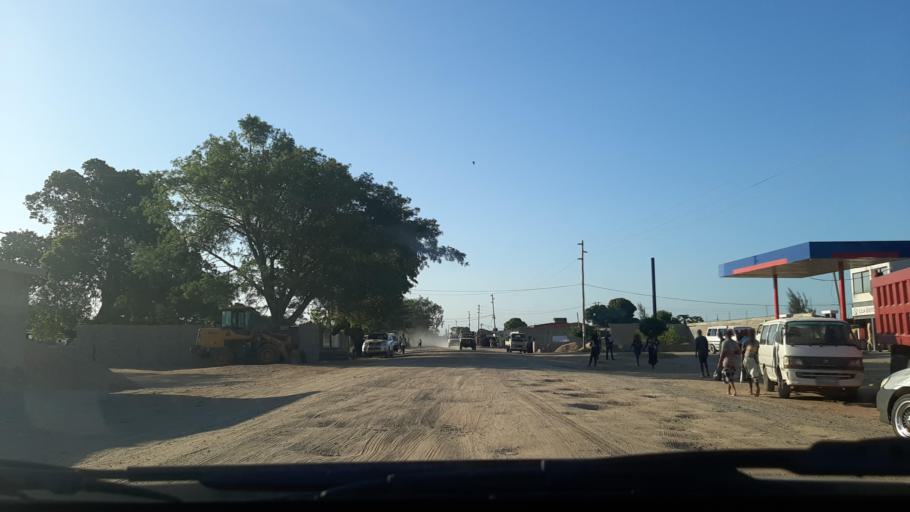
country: MZ
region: Maputo City
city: Maputo
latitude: -25.7352
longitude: 32.5376
